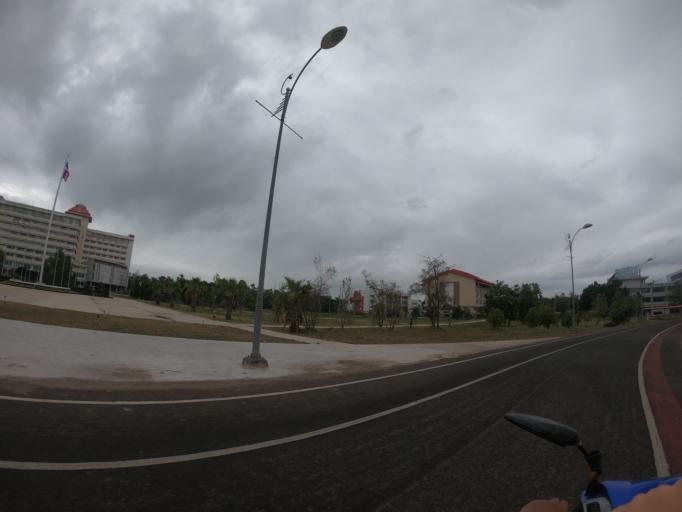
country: TH
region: Roi Et
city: Selaphum
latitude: 16.1420
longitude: 103.8793
